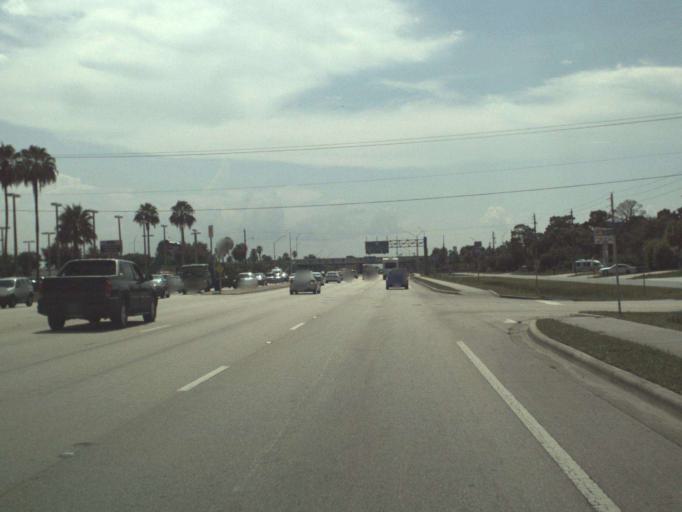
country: US
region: Florida
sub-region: Brevard County
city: Palm Bay
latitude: 27.9987
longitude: -80.6258
